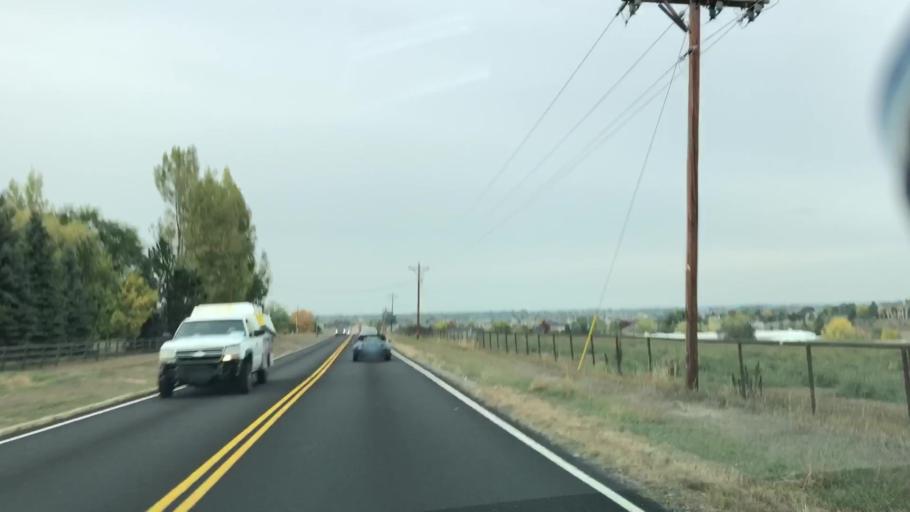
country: US
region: Colorado
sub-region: Larimer County
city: Loveland
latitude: 40.4734
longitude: -105.0583
